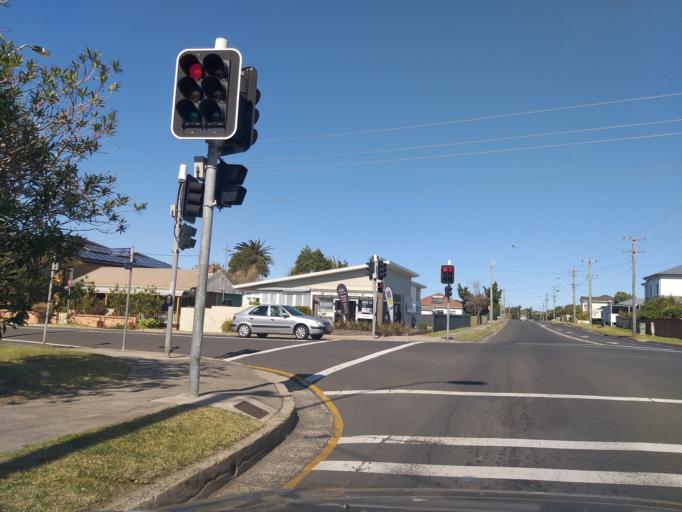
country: AU
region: New South Wales
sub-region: Wollongong
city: Corrimal
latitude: -34.3842
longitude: 150.9069
